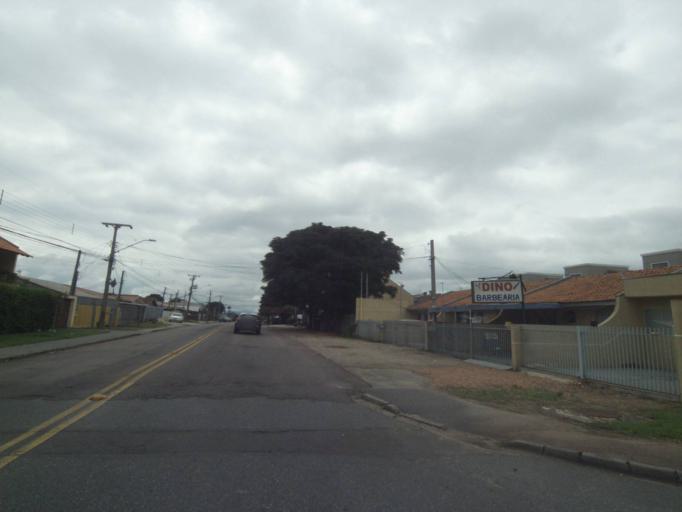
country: BR
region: Parana
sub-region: Pinhais
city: Pinhais
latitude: -25.4539
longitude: -49.2130
